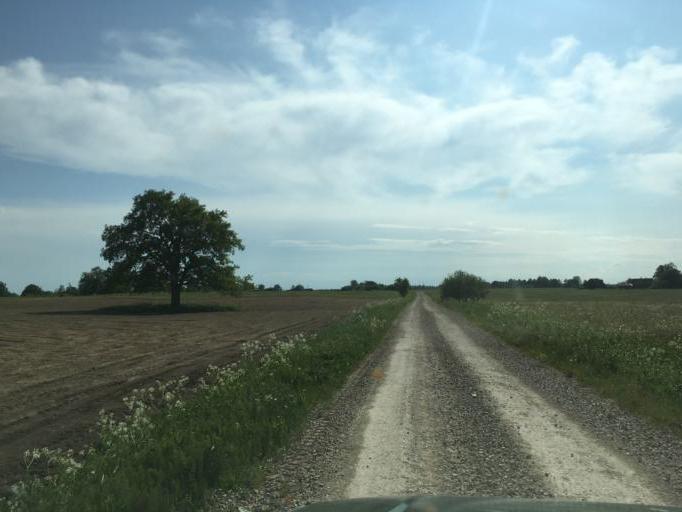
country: LV
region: Dundaga
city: Dundaga
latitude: 57.5548
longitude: 22.4722
